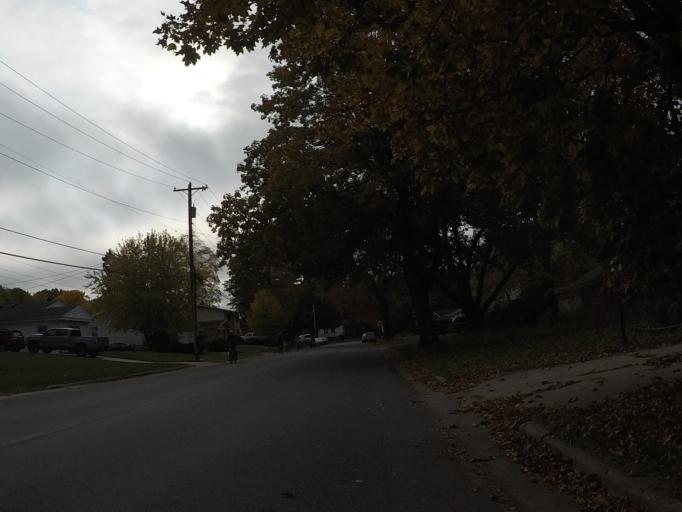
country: US
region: Wisconsin
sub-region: Dane County
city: Maple Bluff
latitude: 43.1318
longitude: -89.3832
